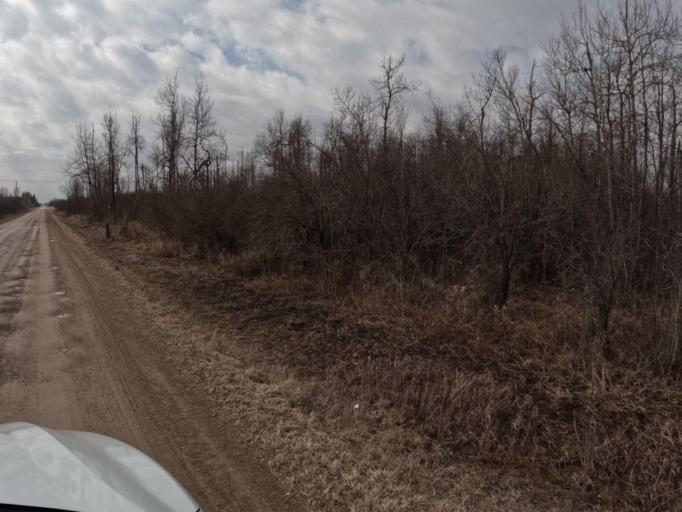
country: CA
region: Ontario
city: Orangeville
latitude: 43.9378
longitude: -80.2219
